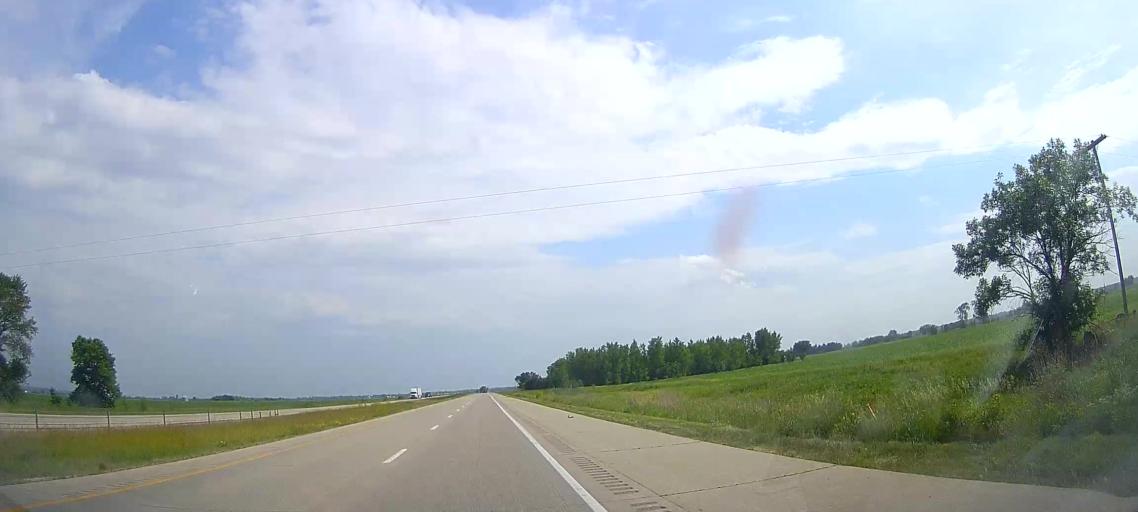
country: US
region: Iowa
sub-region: Monona County
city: Onawa
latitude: 41.8867
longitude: -96.1046
